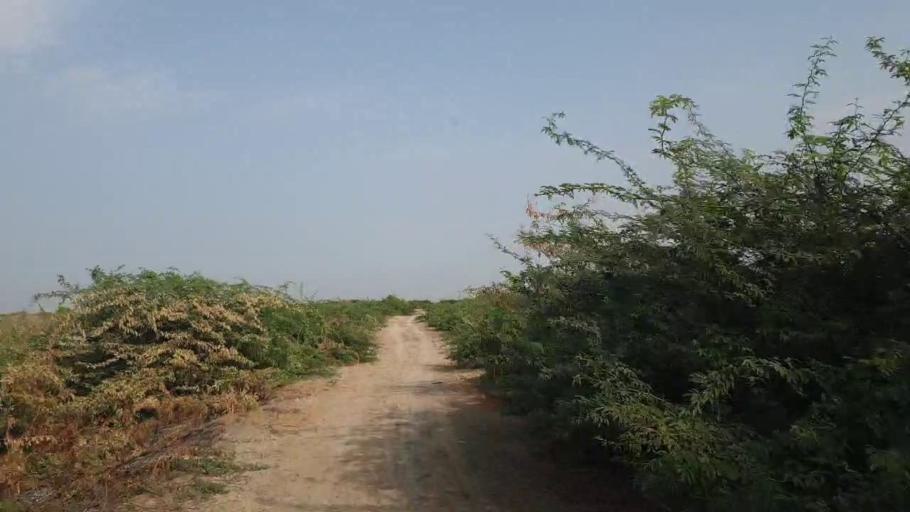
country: PK
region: Sindh
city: Kadhan
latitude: 24.4439
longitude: 68.8033
